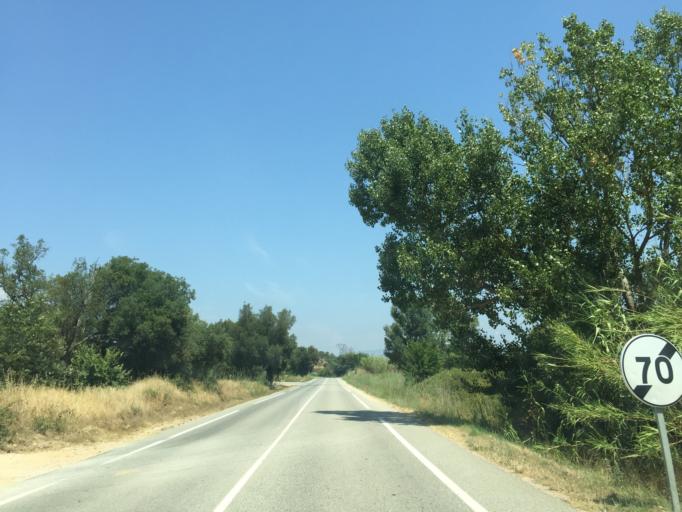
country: FR
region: Provence-Alpes-Cote d'Azur
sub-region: Departement du Var
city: Puget-sur-Argens
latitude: 43.4004
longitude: 6.6776
